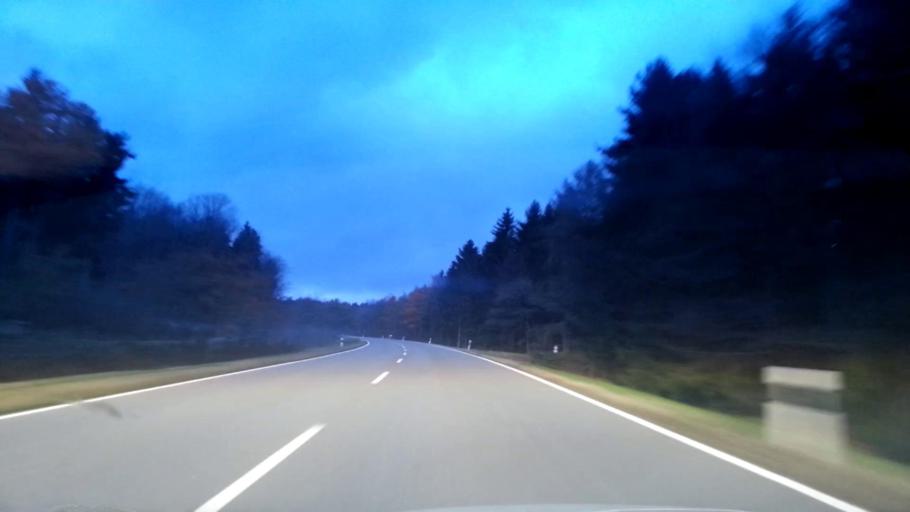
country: DE
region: Bavaria
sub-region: Upper Palatinate
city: Fuchsmuhl
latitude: 49.9352
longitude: 12.1296
